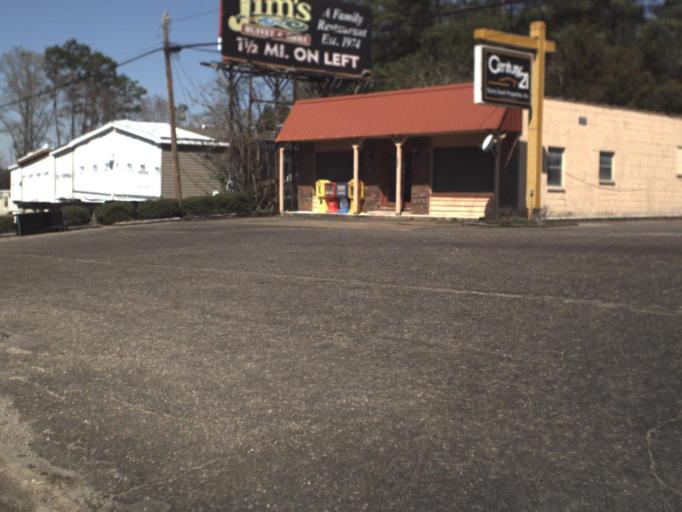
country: US
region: Florida
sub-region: Jackson County
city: Marianna
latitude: 30.7709
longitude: -85.2089
